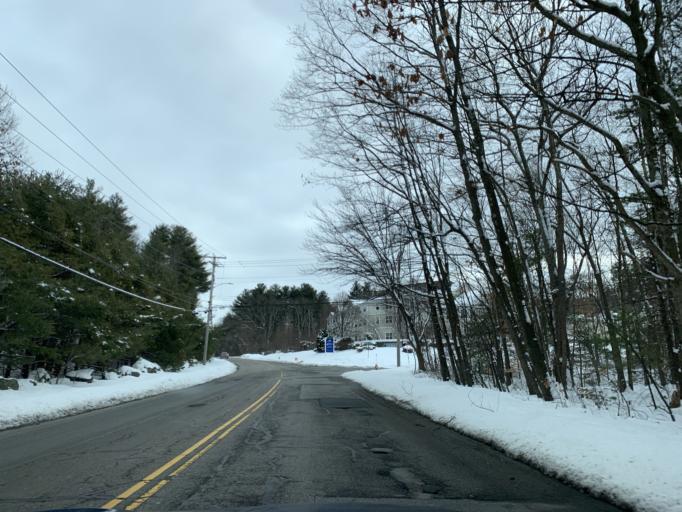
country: US
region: Massachusetts
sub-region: Norfolk County
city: Franklin
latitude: 42.0863
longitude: -71.4269
